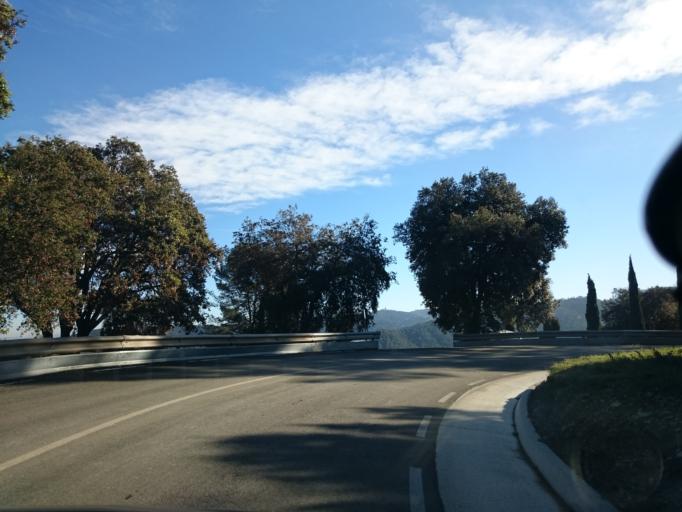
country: ES
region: Catalonia
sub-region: Provincia de Barcelona
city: Sant Cugat del Valles
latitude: 41.4287
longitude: 2.0610
